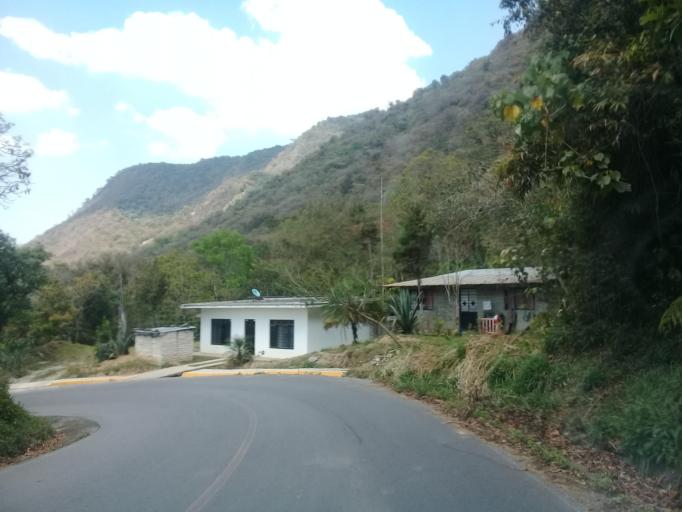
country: MX
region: Veracruz
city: Jalapilla
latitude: 18.8148
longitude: -97.0609
